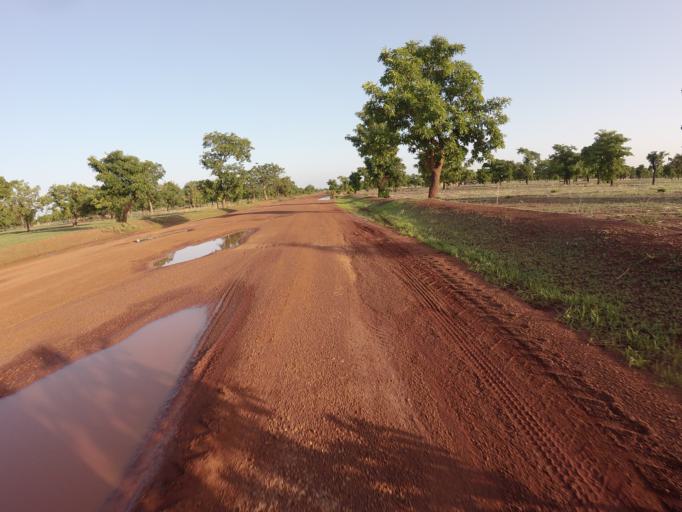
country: TG
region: Savanes
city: Sansanne-Mango
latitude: 10.2778
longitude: -0.0835
